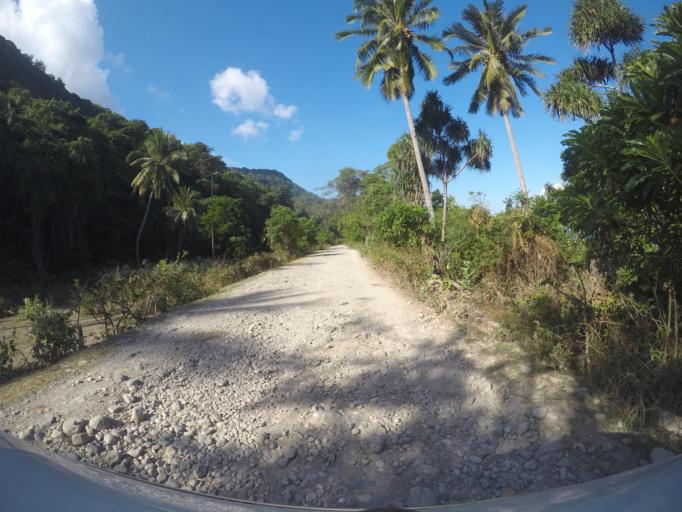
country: TL
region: Viqueque
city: Viqueque
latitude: -8.8008
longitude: 126.5880
